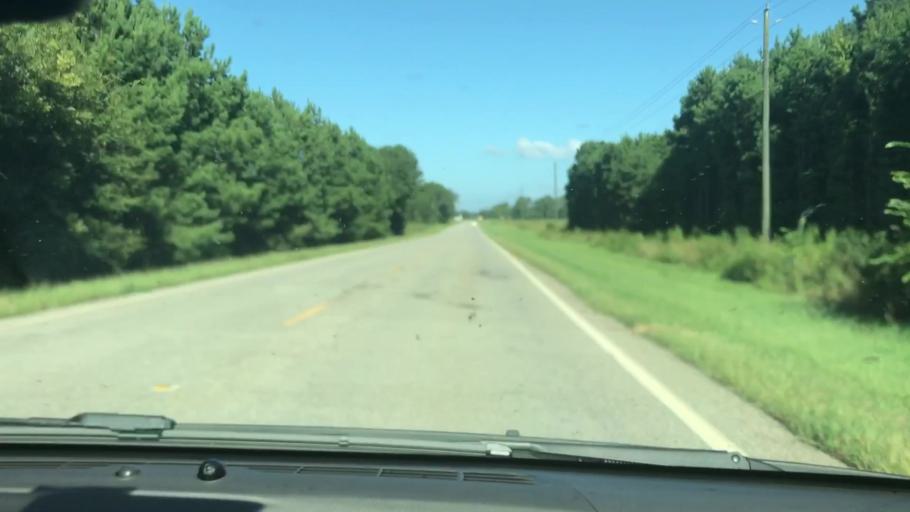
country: US
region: Georgia
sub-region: Quitman County
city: Georgetown
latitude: 31.7574
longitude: -85.0659
